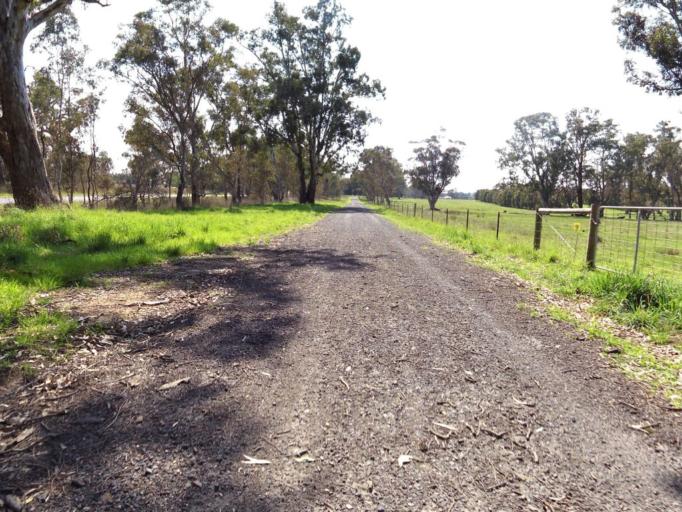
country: AU
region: Victoria
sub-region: Murrindindi
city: Alexandra
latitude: -37.1151
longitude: 145.6068
